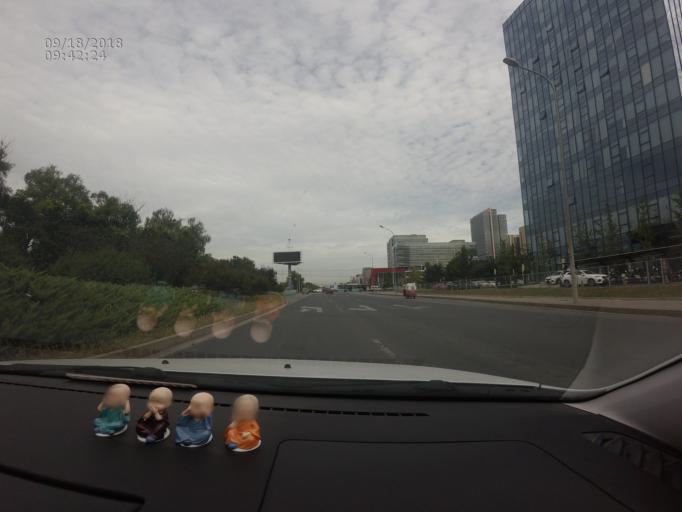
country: CN
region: Beijing
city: Xibeiwang
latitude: 40.0713
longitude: 116.2387
